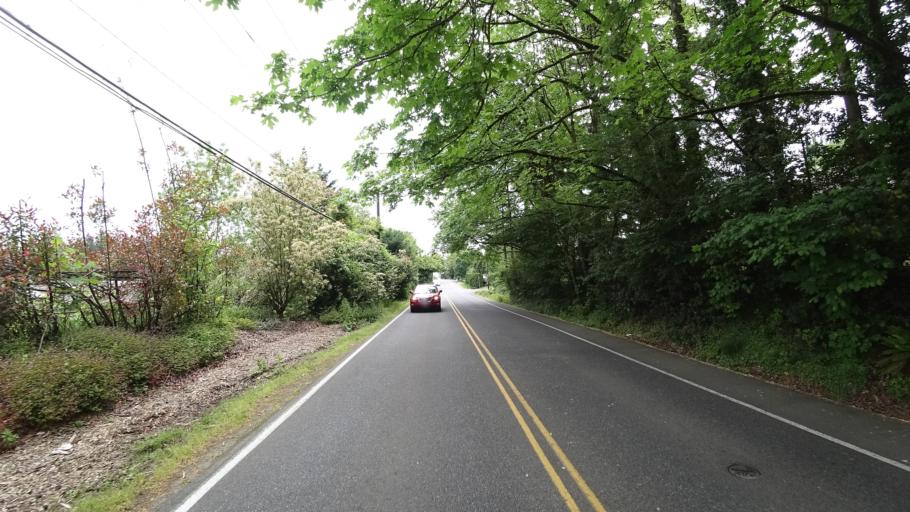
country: US
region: Oregon
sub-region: Washington County
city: Metzger
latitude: 45.4547
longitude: -122.7283
